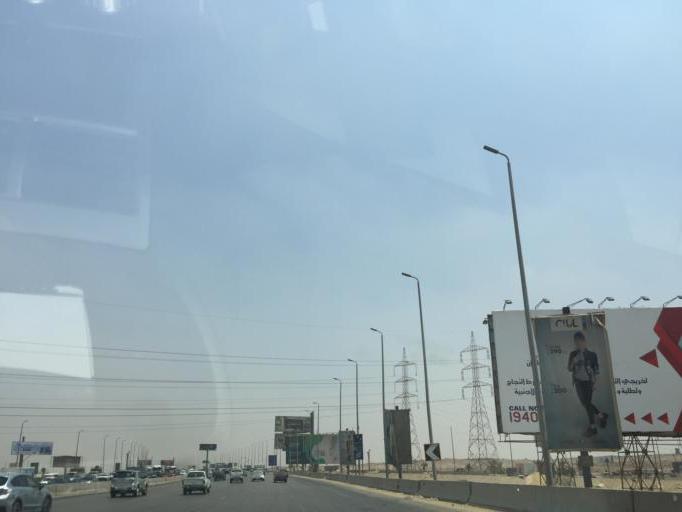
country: EG
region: Muhafazat al Qalyubiyah
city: Al Khankah
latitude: 30.0766
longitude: 31.4341
